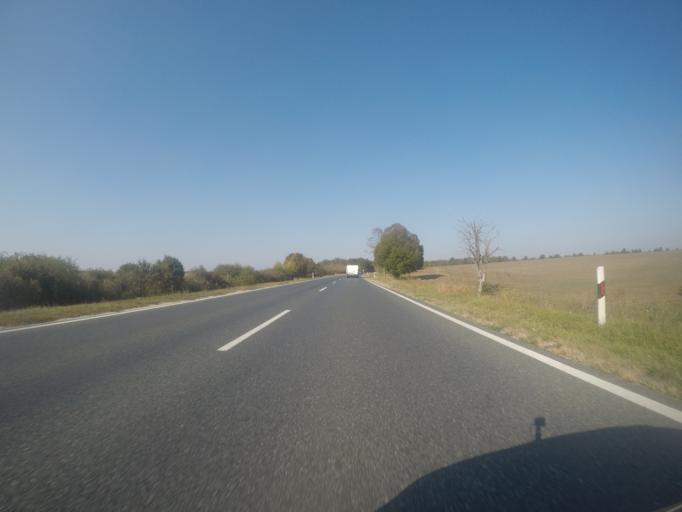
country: HU
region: Tolna
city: Bolcske
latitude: 46.7309
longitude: 18.8825
